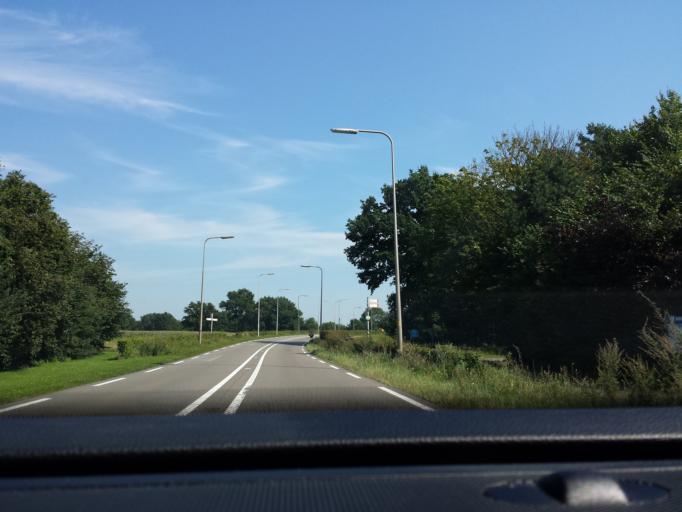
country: NL
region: Overijssel
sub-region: Gemeente Hof van Twente
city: Hengevelde
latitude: 52.2503
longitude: 6.6457
